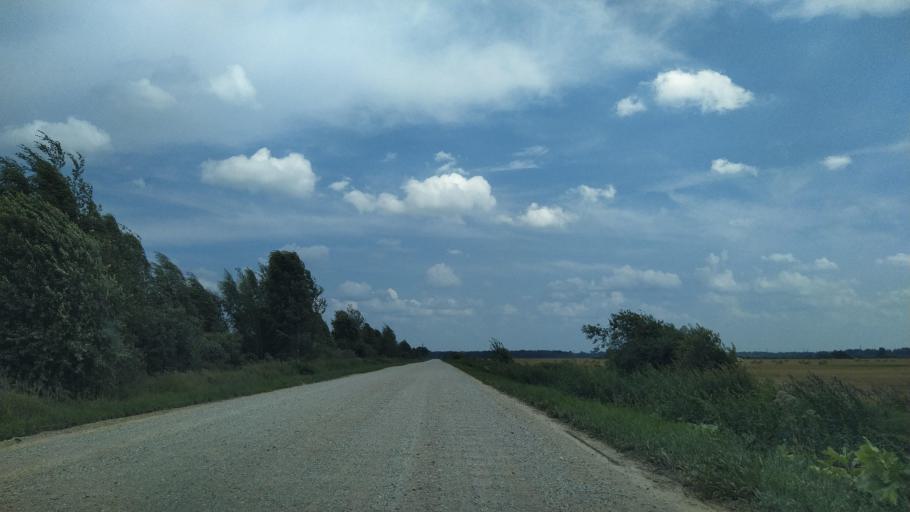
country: RU
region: Pskov
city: Pskov
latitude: 57.5851
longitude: 28.3305
